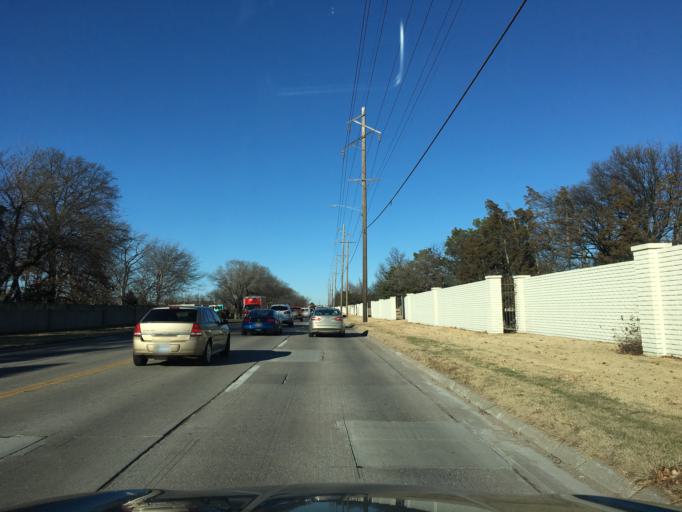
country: US
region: Kansas
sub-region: Sedgwick County
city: Bellaire
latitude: 37.7020
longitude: -97.2446
